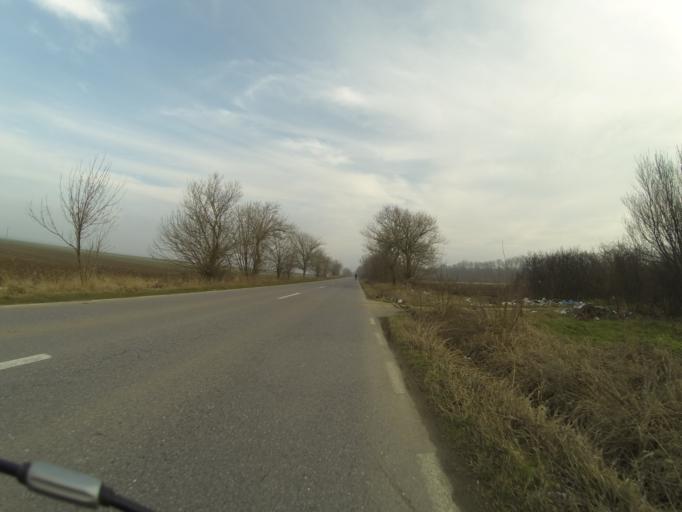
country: RO
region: Mehedinti
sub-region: Comuna Corlatel
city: Corlatel
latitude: 44.4044
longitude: 22.8989
